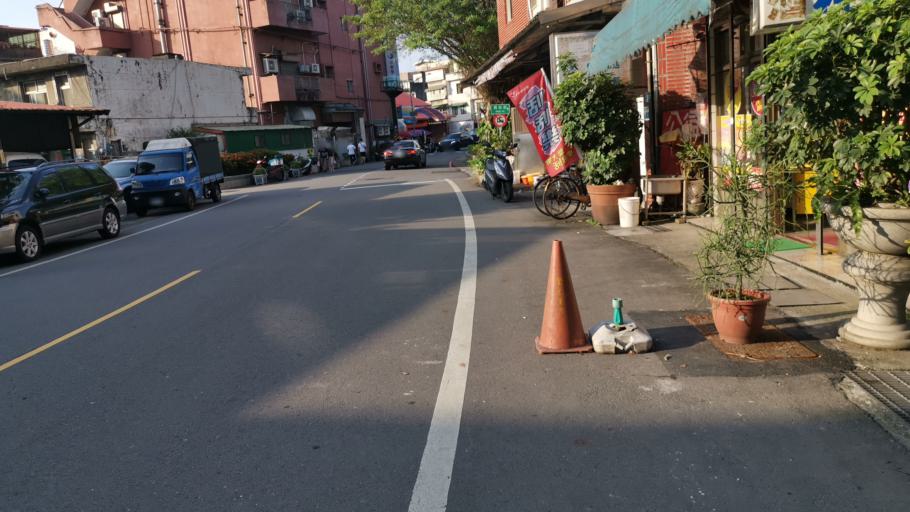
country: TW
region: Taiwan
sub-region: Keelung
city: Keelung
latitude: 25.2197
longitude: 121.6401
